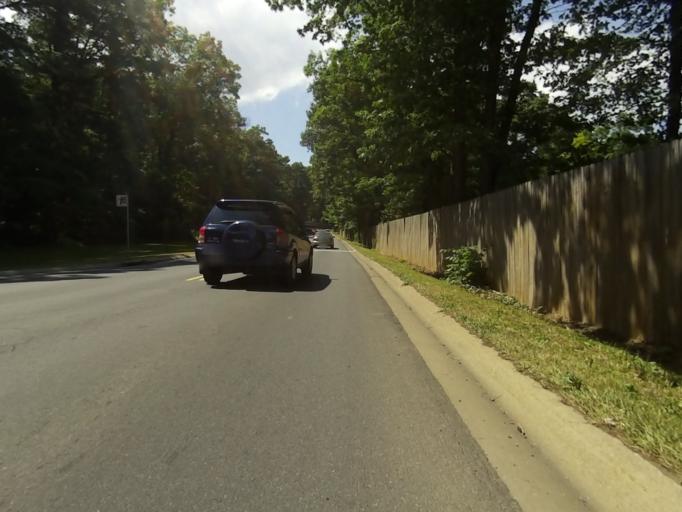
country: US
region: Pennsylvania
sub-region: Centre County
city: Park Forest Village
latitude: 40.7934
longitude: -77.9104
